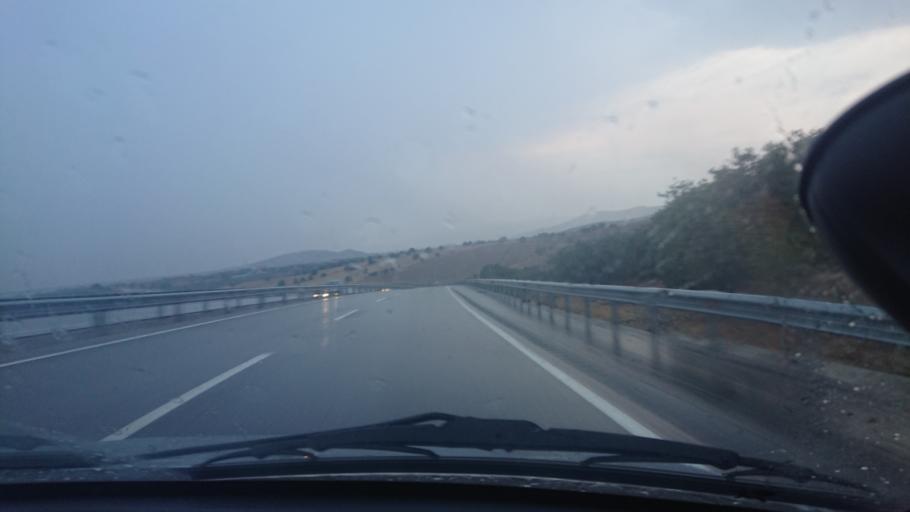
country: TR
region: Manisa
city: Menye
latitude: 38.5304
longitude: 28.4131
